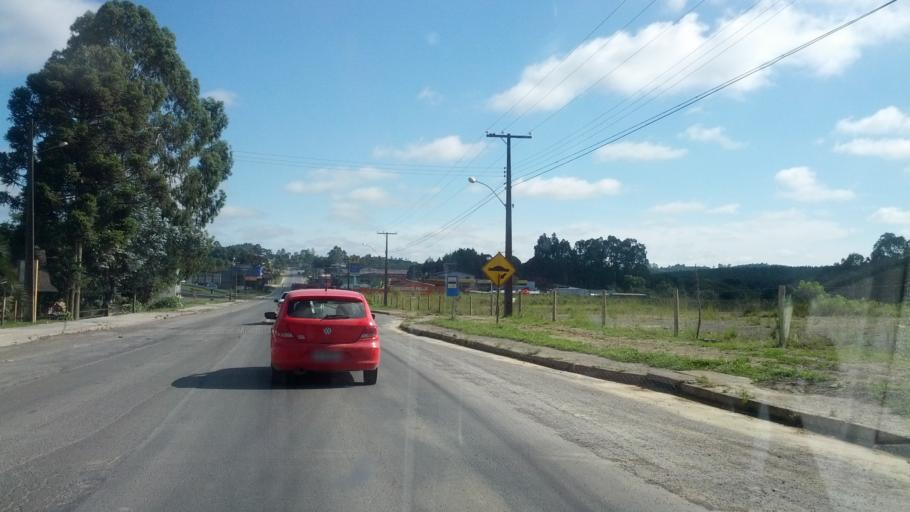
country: BR
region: Santa Catarina
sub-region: Otacilio Costa
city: Otacilio Costa
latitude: -27.4962
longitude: -50.1217
